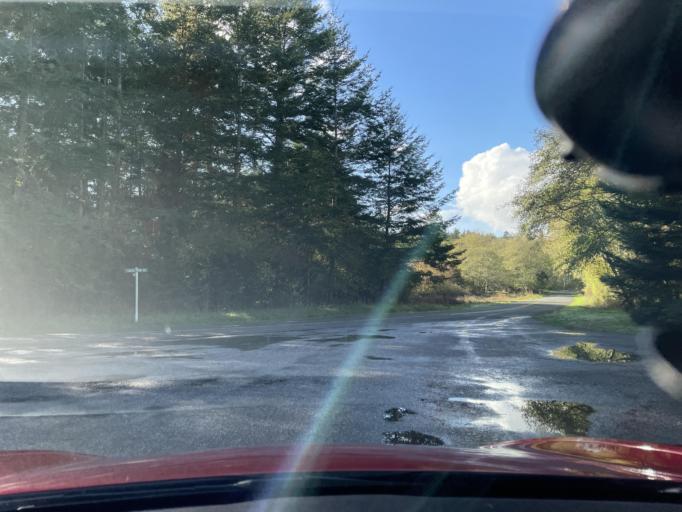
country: US
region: Washington
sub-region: San Juan County
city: Friday Harbor
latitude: 48.4596
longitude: -122.9660
